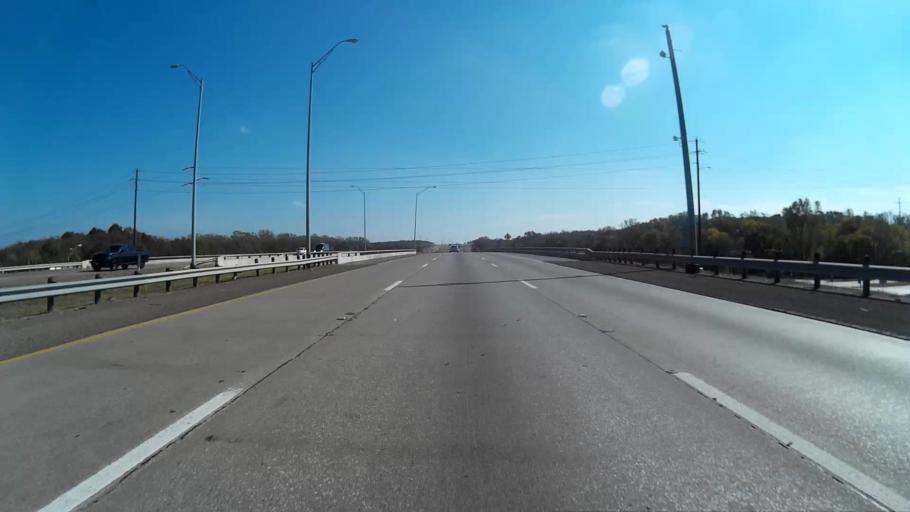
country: US
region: Texas
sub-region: Dallas County
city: Hutchins
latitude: 32.6821
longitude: -96.7449
